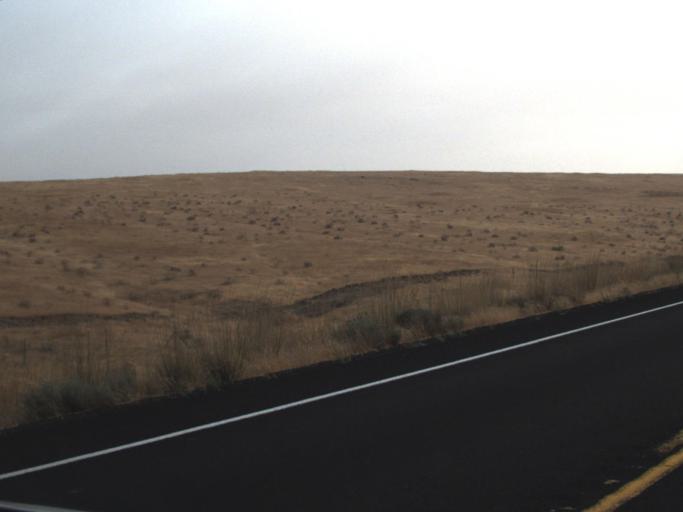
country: US
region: Washington
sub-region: Yakima County
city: Toppenish
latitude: 46.2775
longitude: -120.3883
